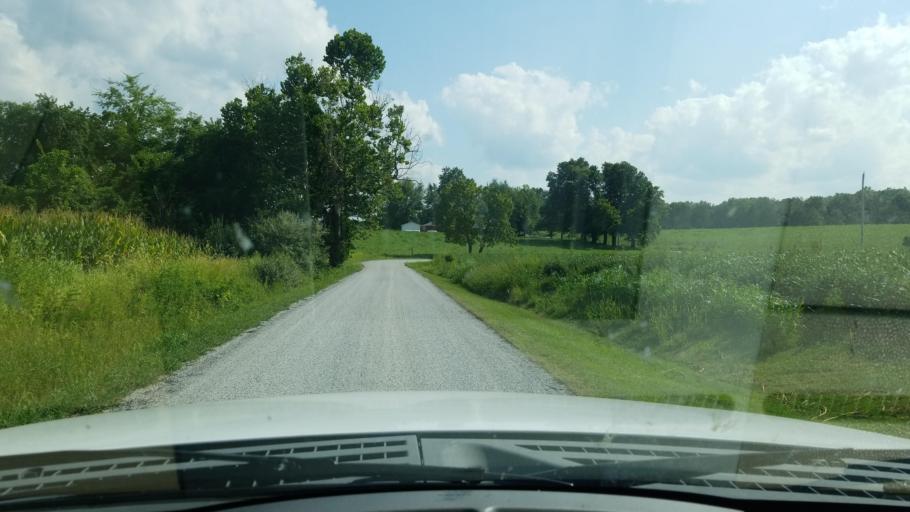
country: US
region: Illinois
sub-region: Saline County
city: Eldorado
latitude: 37.8423
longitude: -88.4802
